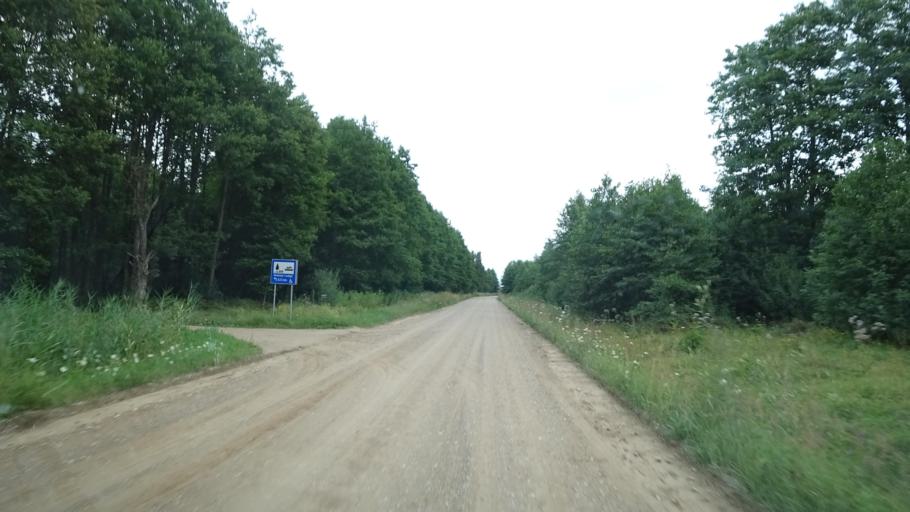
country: LV
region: Liepaja
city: Vec-Liepaja
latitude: 56.6238
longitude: 21.0444
